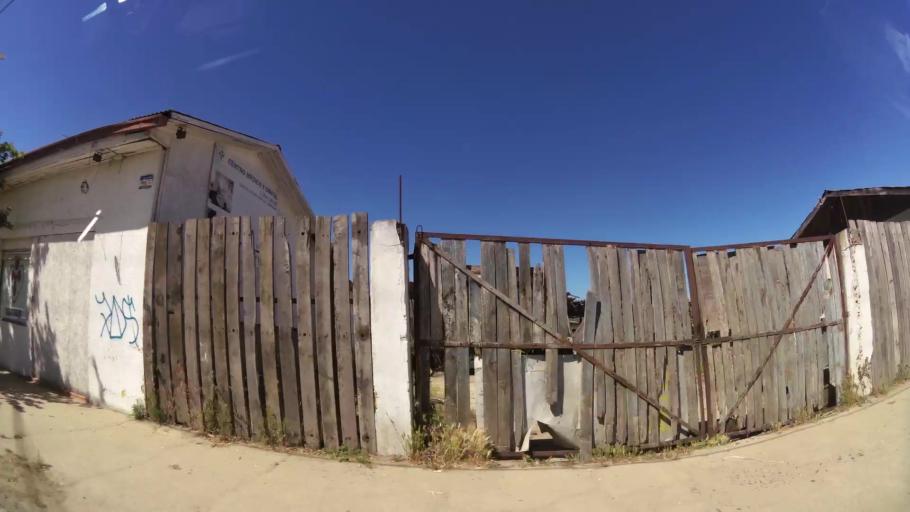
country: CL
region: Valparaiso
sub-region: Provincia de Marga Marga
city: Quilpue
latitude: -33.3240
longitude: -71.4035
